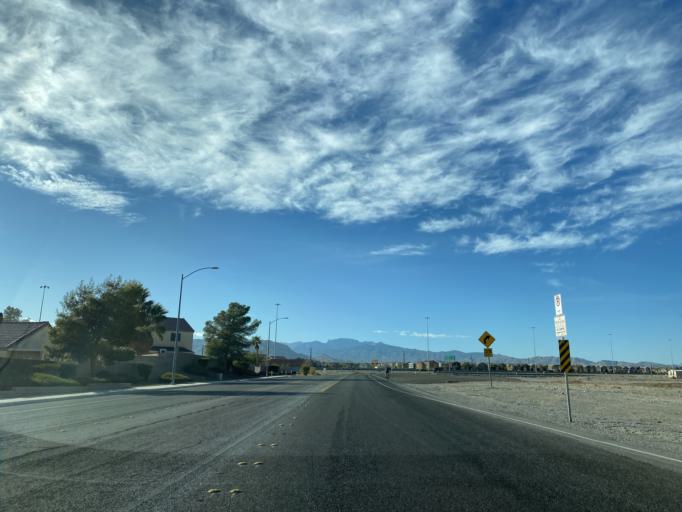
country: US
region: Nevada
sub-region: Clark County
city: Summerlin South
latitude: 36.3065
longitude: -115.2902
